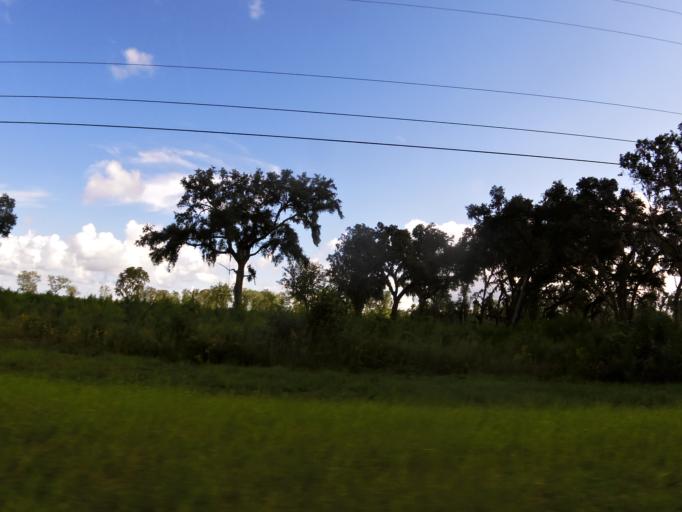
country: US
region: Georgia
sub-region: Glynn County
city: Brunswick
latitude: 31.1058
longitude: -81.6314
